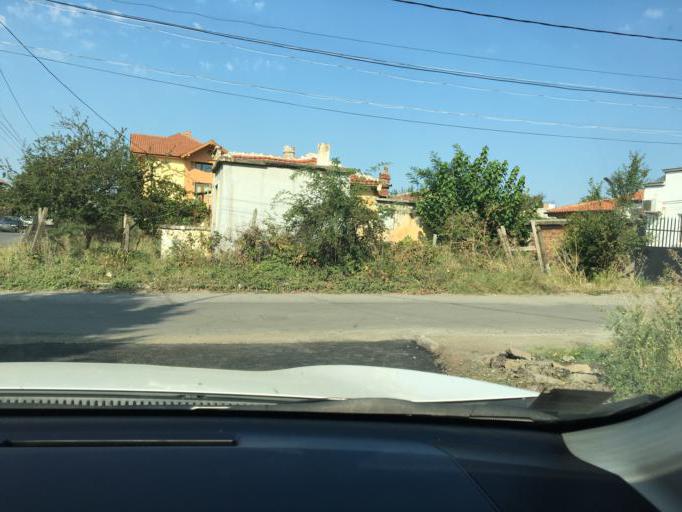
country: BG
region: Burgas
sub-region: Obshtina Burgas
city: Burgas
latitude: 42.6143
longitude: 27.4879
